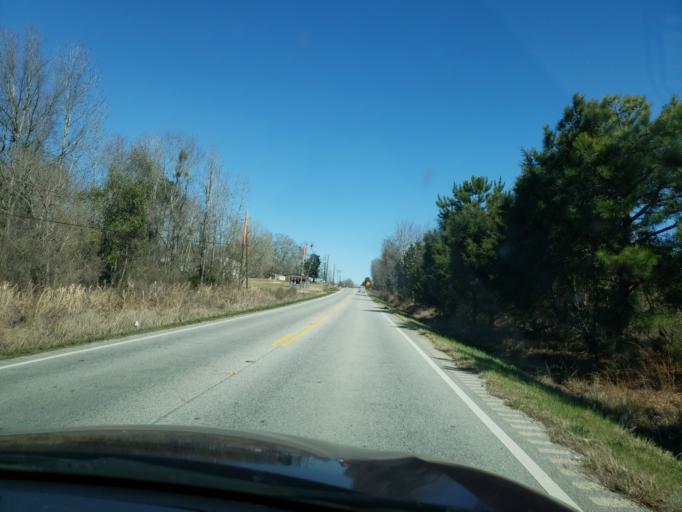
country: US
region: Alabama
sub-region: Lee County
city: Auburn
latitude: 32.5976
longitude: -85.6135
